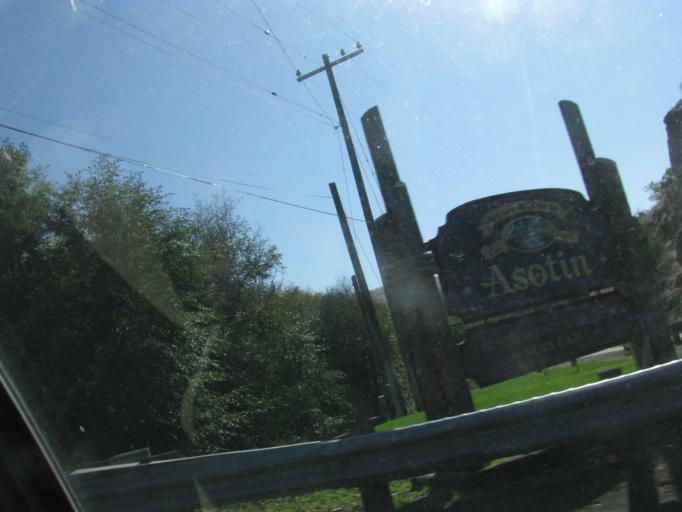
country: US
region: Washington
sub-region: Asotin County
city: Asotin
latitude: 46.3418
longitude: -117.0560
